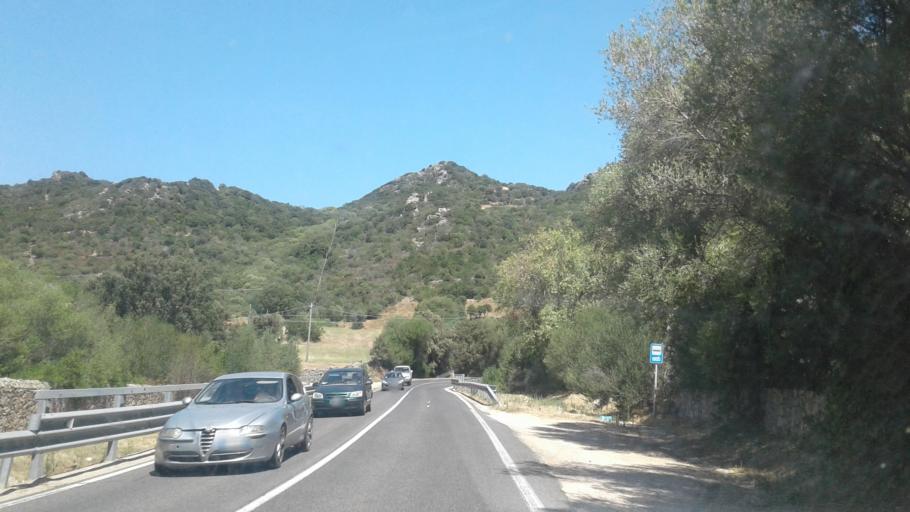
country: IT
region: Sardinia
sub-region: Provincia di Olbia-Tempio
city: Telti
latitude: 40.9039
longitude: 9.3938
